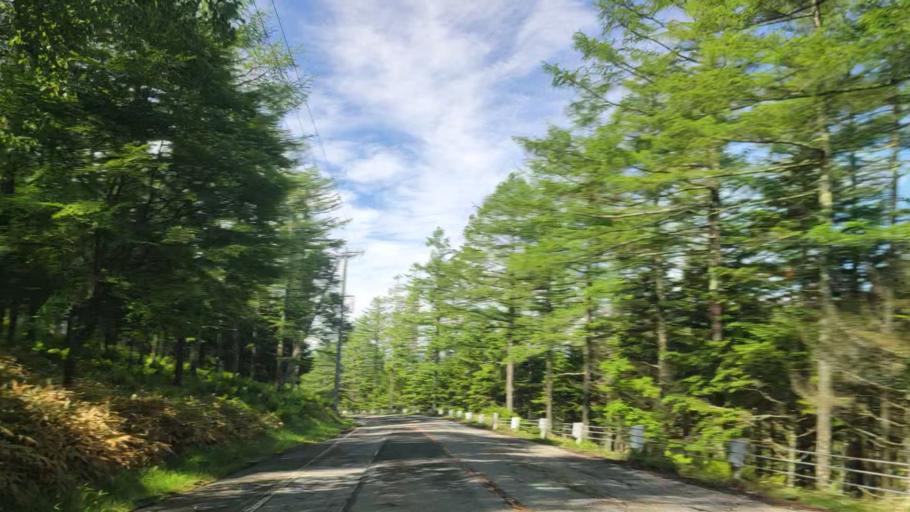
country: JP
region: Nagano
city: Suwa
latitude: 36.0991
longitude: 138.1527
